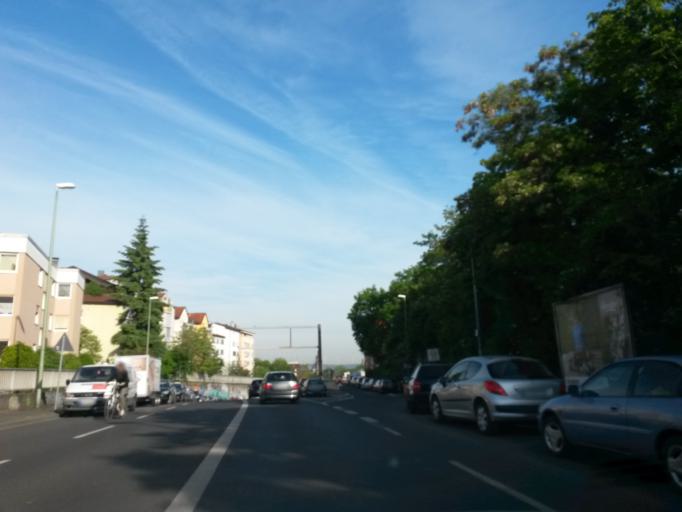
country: DE
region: Bavaria
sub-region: Regierungsbezirk Unterfranken
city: Wuerzburg
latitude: 49.7860
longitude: 9.9453
